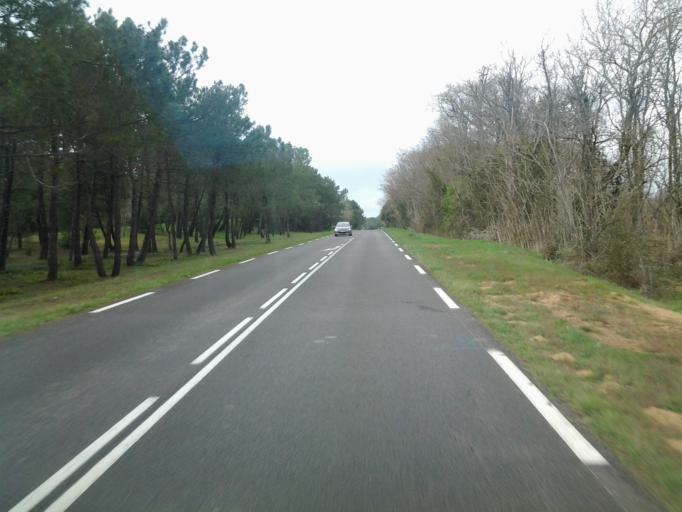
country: FR
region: Pays de la Loire
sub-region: Departement de la Vendee
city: La Tranche-sur-Mer
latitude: 46.3691
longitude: -1.4593
